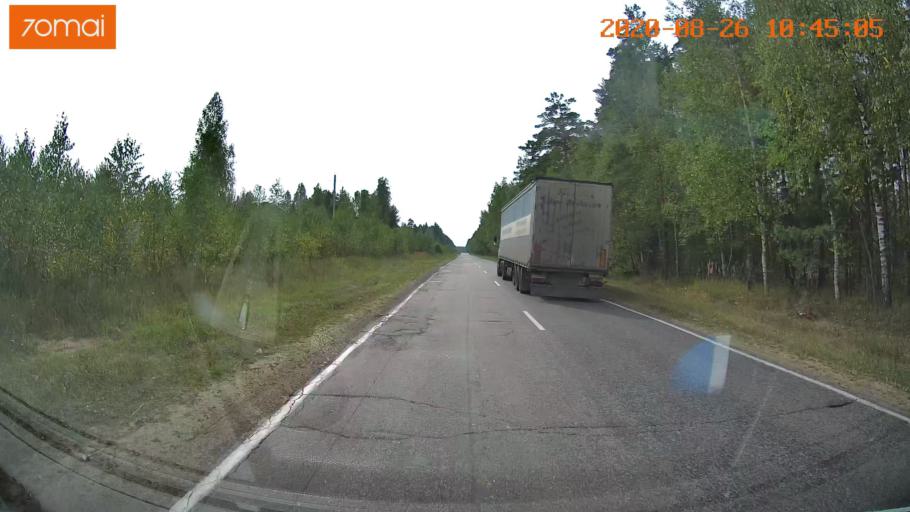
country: RU
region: Rjazan
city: Lashma
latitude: 54.7618
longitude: 41.1848
